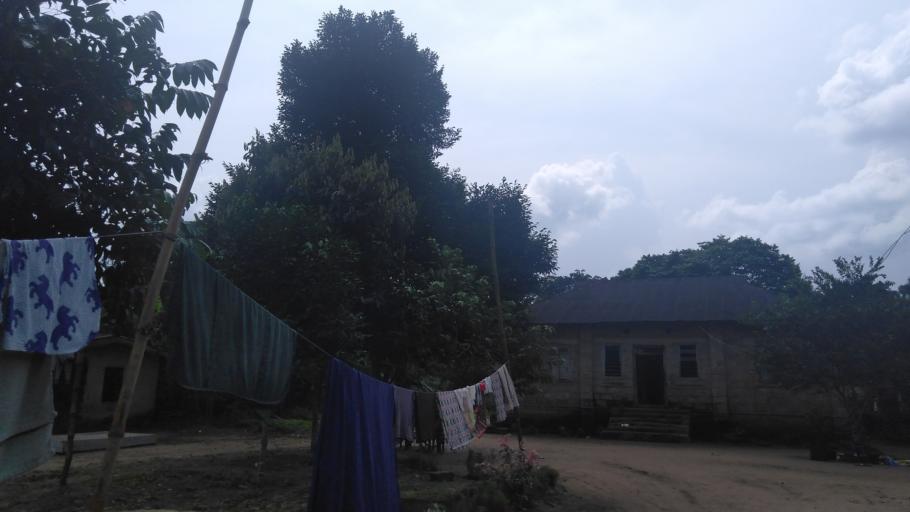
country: NG
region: Abia
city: Aba
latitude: 5.0459
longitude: 7.2397
